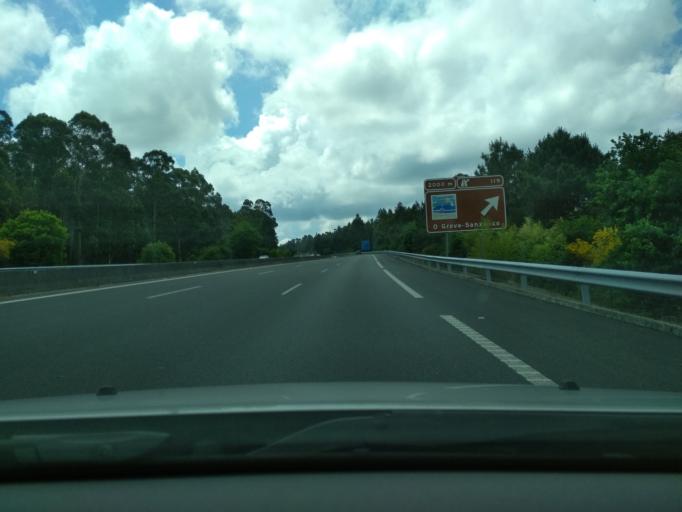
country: ES
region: Galicia
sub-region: Provincia de Pontevedra
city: Barro
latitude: 42.5366
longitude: -8.6689
